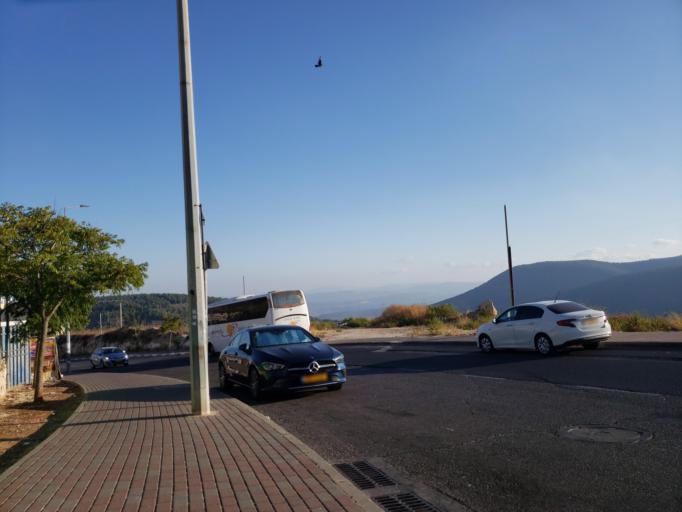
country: IL
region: Northern District
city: Safed
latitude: 32.9659
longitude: 35.4869
